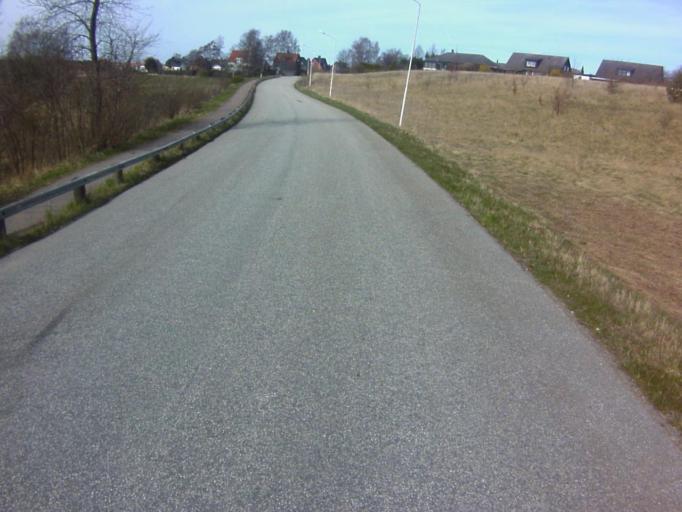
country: SE
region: Skane
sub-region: Kavlinge Kommun
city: Kaevlinge
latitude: 55.7760
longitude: 13.1098
